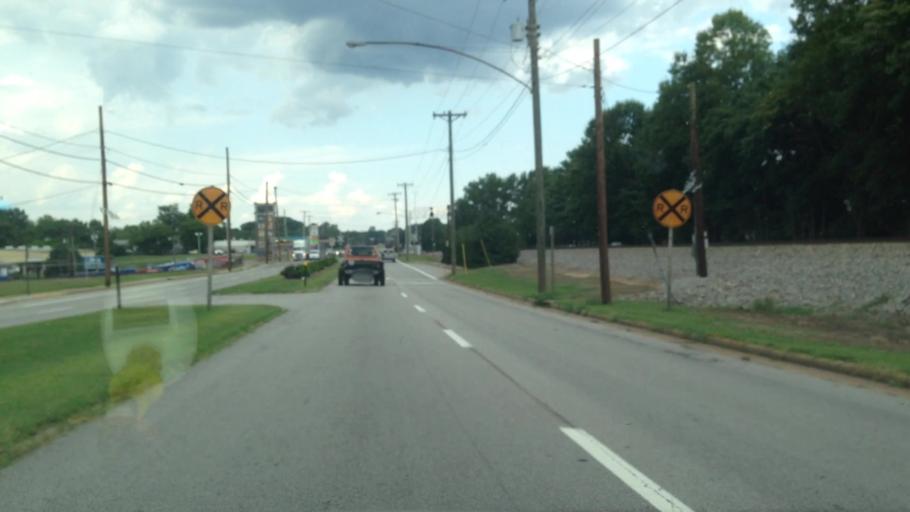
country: US
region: Virginia
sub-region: City of Danville
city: Danville
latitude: 36.5493
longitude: -79.4608
